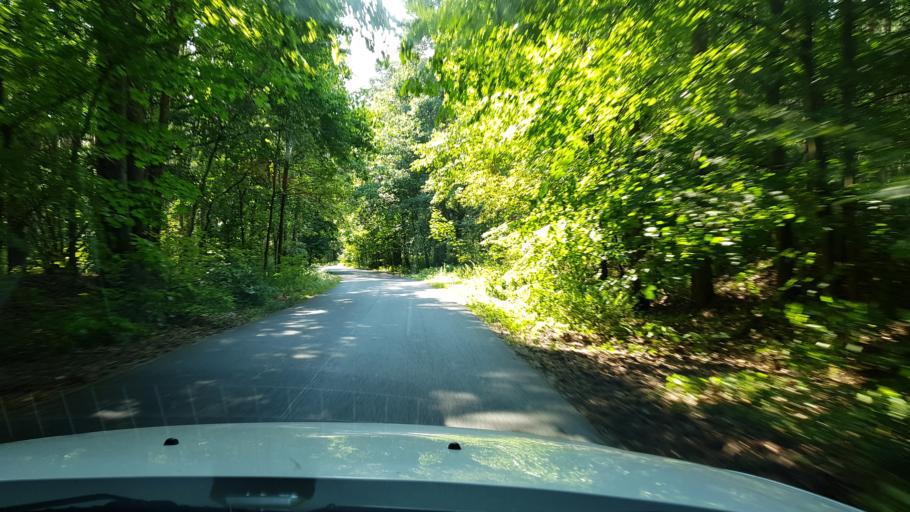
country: PL
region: West Pomeranian Voivodeship
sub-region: Powiat gryfinski
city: Chojna
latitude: 52.9404
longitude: 14.5143
